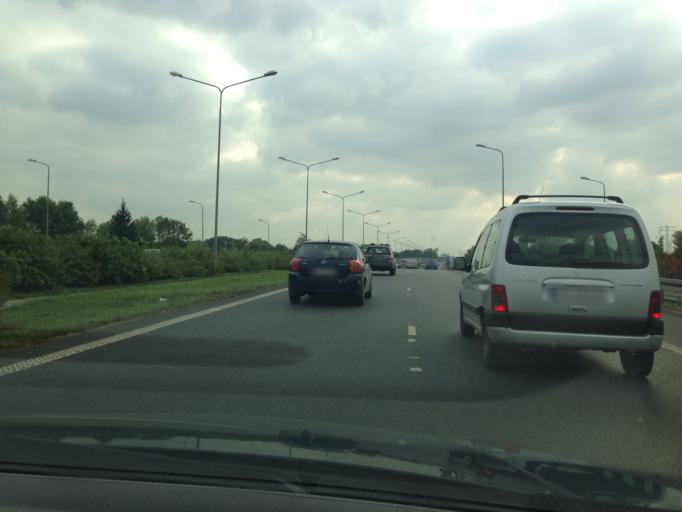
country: PL
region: Greater Poland Voivodeship
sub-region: Powiat poznanski
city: Lubon
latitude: 52.3699
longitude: 16.8626
